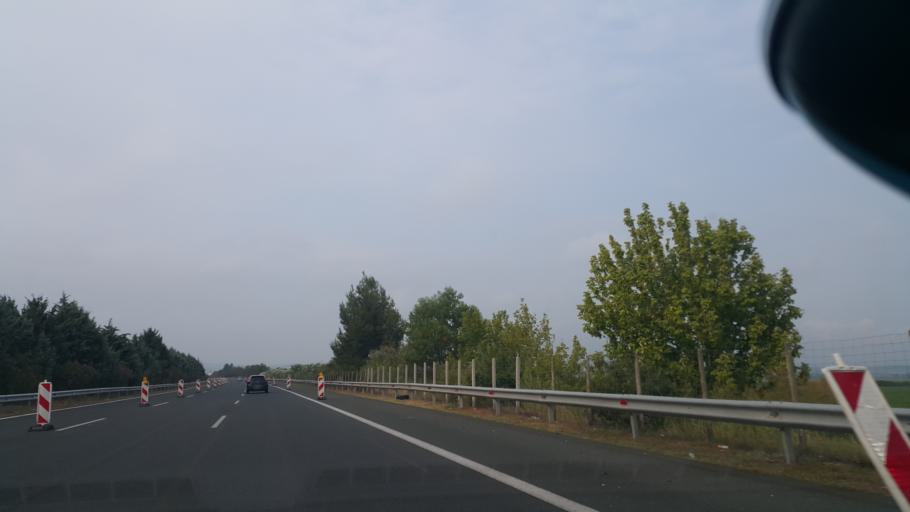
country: GR
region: Central Macedonia
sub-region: Nomos Imathias
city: Kleidi
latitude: 40.5350
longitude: 22.5798
